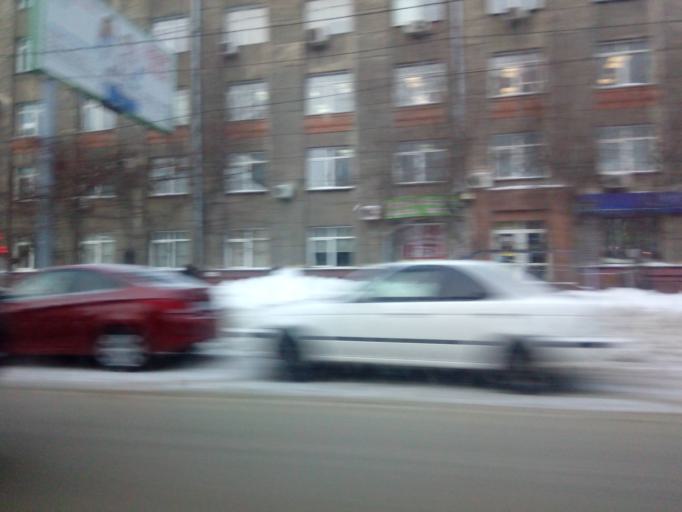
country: RU
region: Novosibirsk
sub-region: Novosibirskiy Rayon
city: Novosibirsk
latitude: 55.0315
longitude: 82.9130
